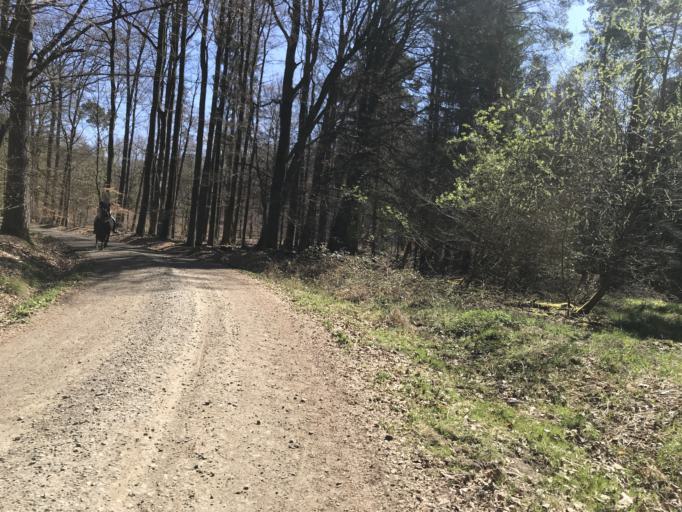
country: DE
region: Hesse
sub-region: Regierungsbezirk Giessen
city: Alten Buseck
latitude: 50.6431
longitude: 8.7537
